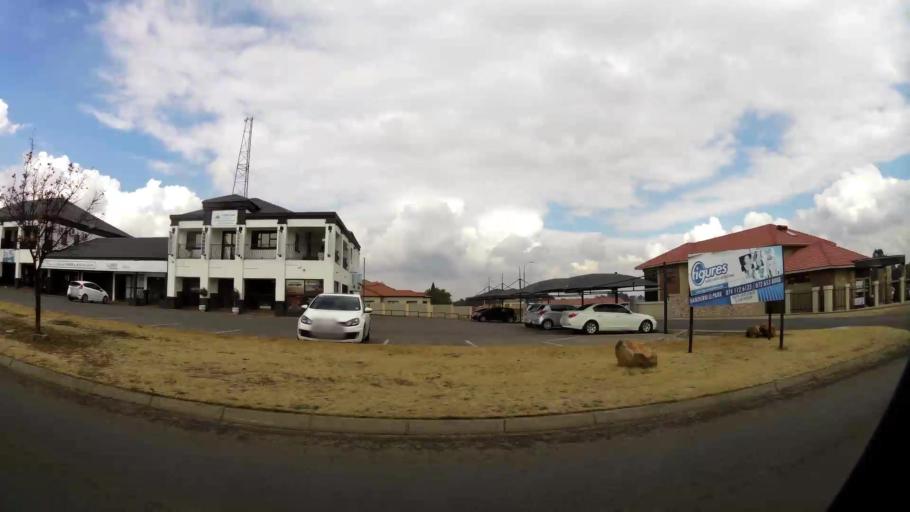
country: ZA
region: Gauteng
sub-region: Sedibeng District Municipality
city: Vanderbijlpark
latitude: -26.7298
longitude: 27.8599
